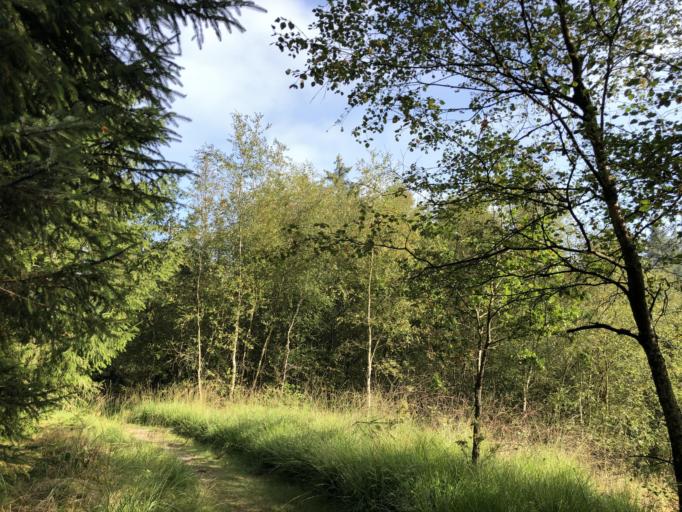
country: DK
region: Central Jutland
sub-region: Lemvig Kommune
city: Lemvig
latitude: 56.4689
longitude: 8.3278
